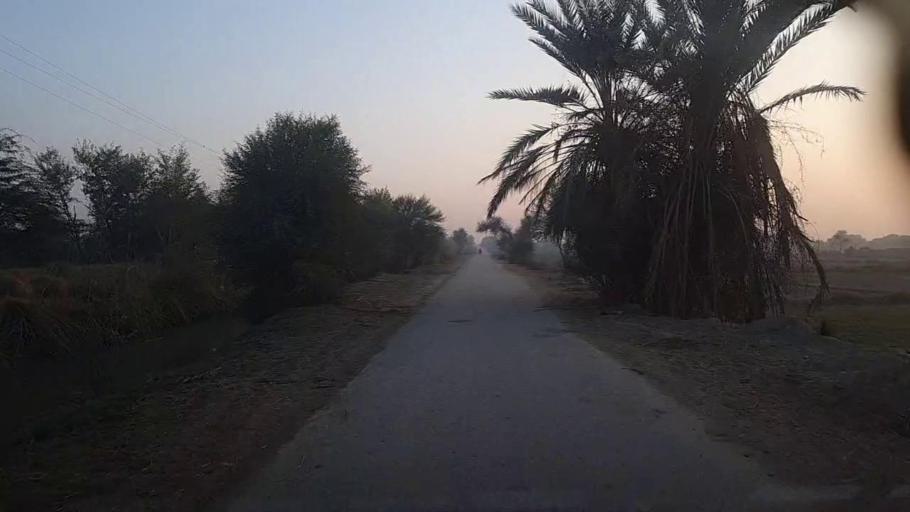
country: PK
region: Sindh
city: Karaundi
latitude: 26.8434
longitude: 68.3707
